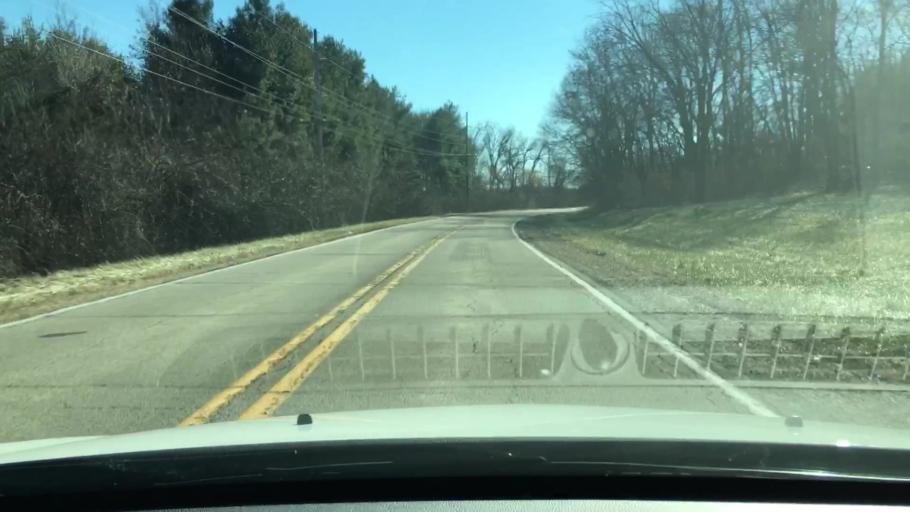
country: US
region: Illinois
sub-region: Fulton County
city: Astoria
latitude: 40.2036
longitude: -90.2027
